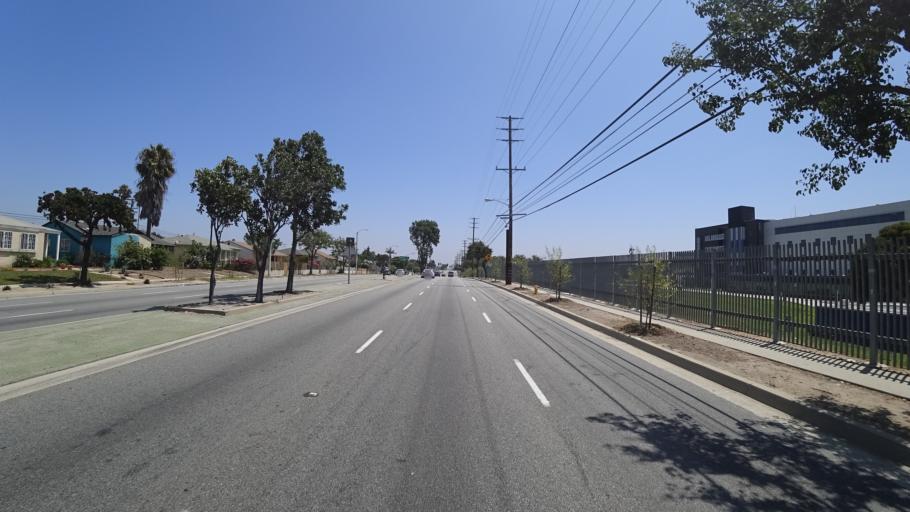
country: US
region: California
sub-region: Los Angeles County
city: West Athens
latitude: 33.9309
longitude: -118.3068
